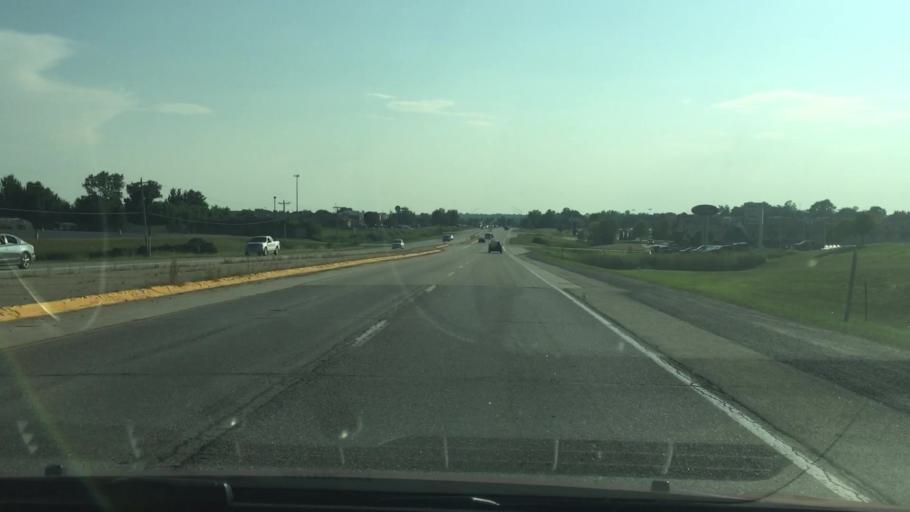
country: US
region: Iowa
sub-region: Muscatine County
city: Muscatine
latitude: 41.4592
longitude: -91.0183
